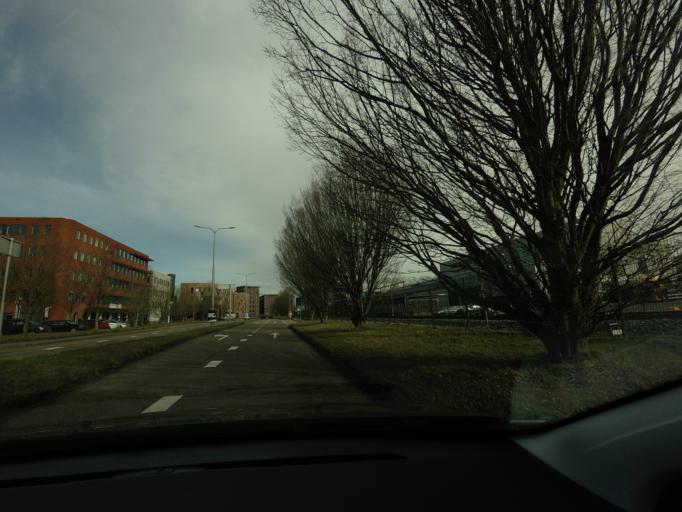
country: NL
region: Friesland
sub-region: Gemeente Leeuwarden
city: Leeuwarden
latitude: 53.1972
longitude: 5.7997
